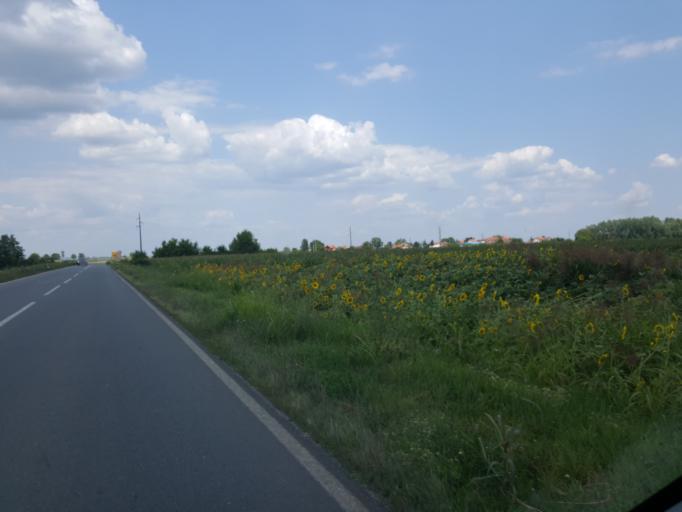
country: RS
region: Autonomna Pokrajina Vojvodina
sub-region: Sremski Okrug
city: Pecinci
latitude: 44.9123
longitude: 19.9567
